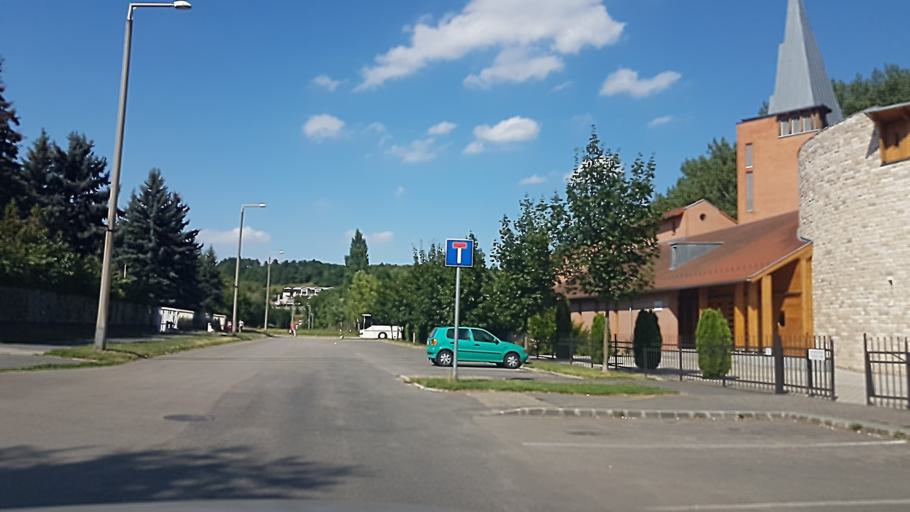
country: HU
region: Gyor-Moson-Sopron
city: Sopron
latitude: 47.6935
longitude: 16.5774
